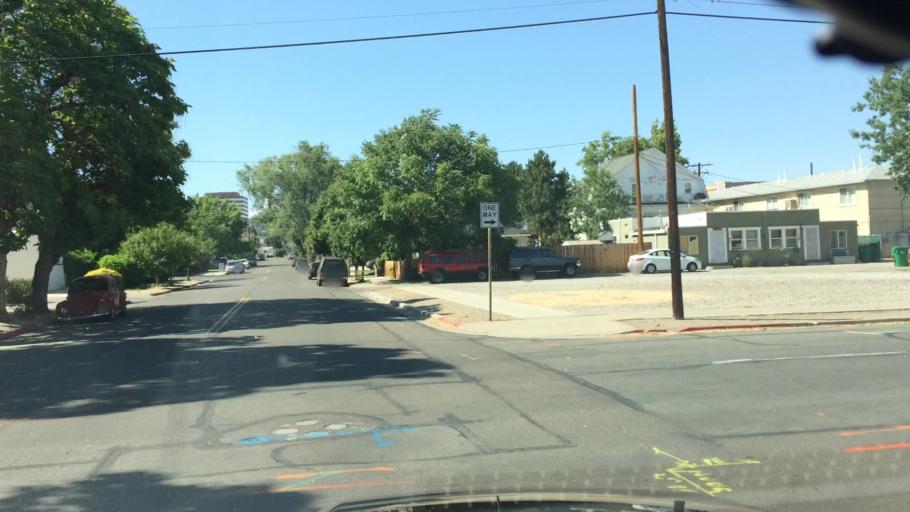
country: US
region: Nevada
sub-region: Washoe County
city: Reno
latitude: 39.5143
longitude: -119.8088
